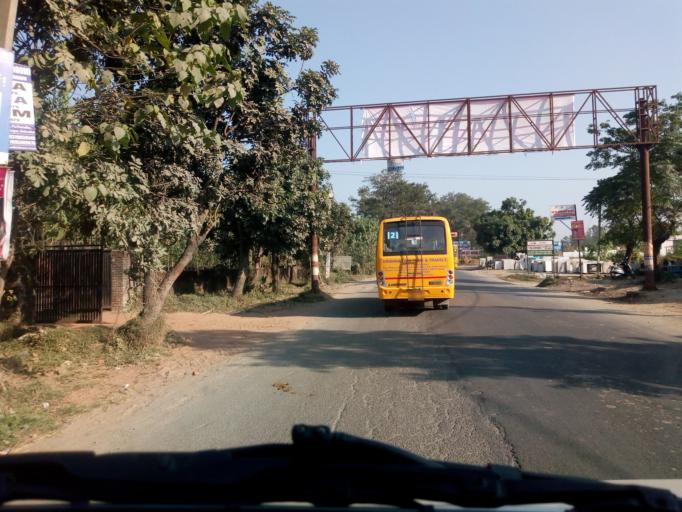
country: IN
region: Uttarakhand
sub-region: Dehradun
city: Vikasnagar
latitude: 30.3505
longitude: 77.8662
